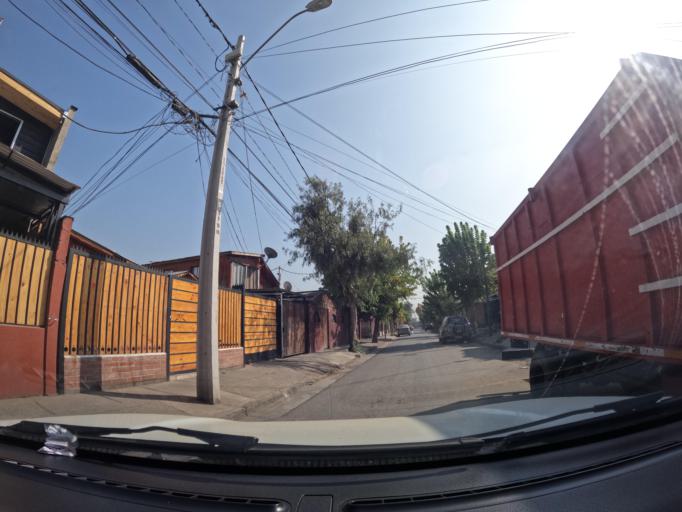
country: CL
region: Santiago Metropolitan
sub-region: Provincia de Santiago
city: Villa Presidente Frei, Nunoa, Santiago, Chile
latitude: -33.4802
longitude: -70.5624
